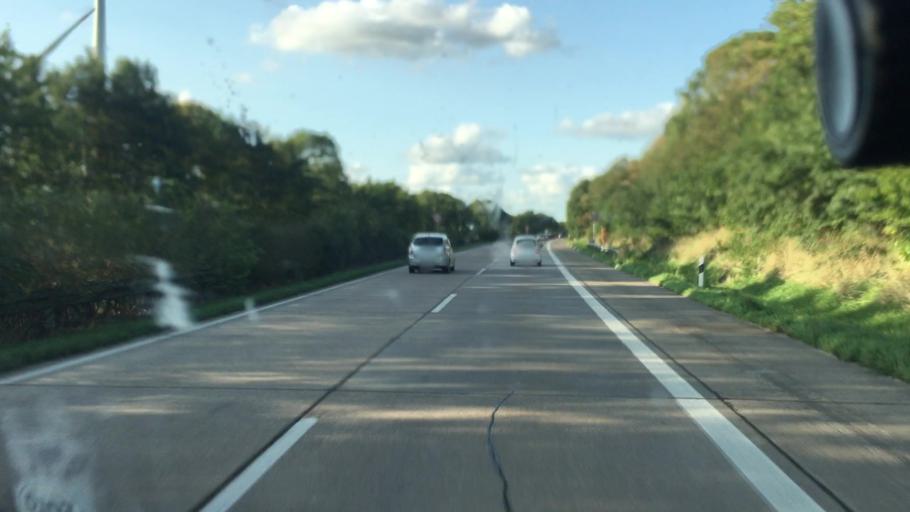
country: DE
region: Lower Saxony
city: Sande
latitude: 53.5025
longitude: 7.9960
